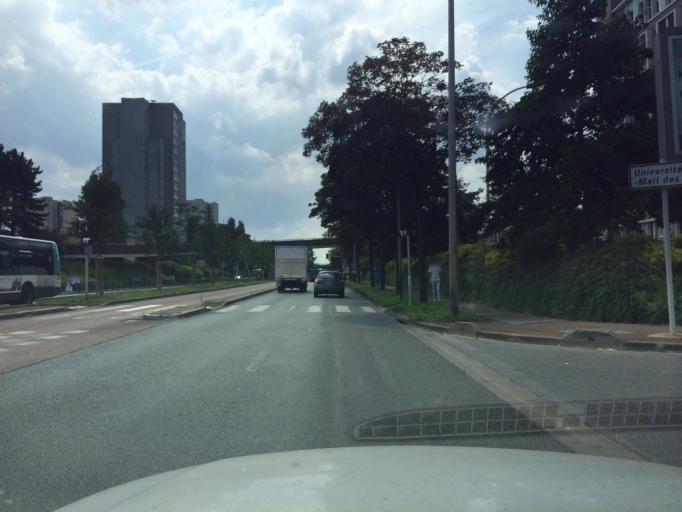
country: FR
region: Ile-de-France
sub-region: Departement du Val-de-Marne
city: Creteil
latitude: 48.7879
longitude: 2.4507
